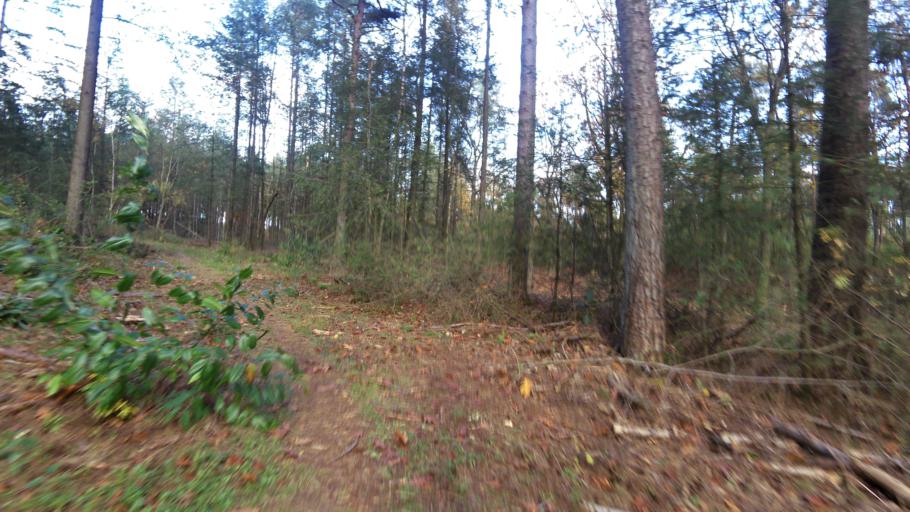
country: NL
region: Gelderland
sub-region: Gemeente Heerde
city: Heerde
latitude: 52.4189
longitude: 6.0396
